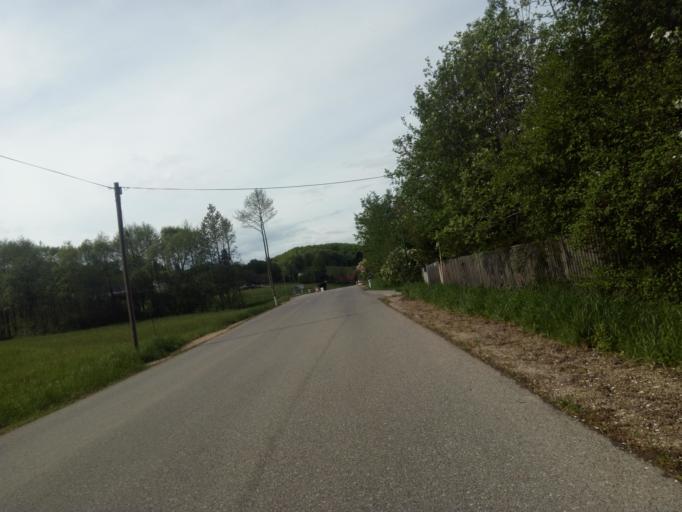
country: AT
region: Lower Austria
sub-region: Politischer Bezirk Wien-Umgebung
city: Wolfsgraben
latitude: 48.1234
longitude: 16.0963
